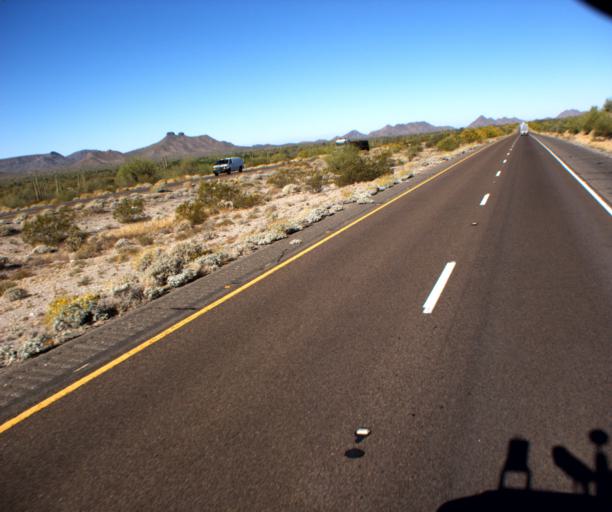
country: US
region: Arizona
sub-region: Maricopa County
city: Gila Bend
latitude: 32.8639
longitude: -112.4077
